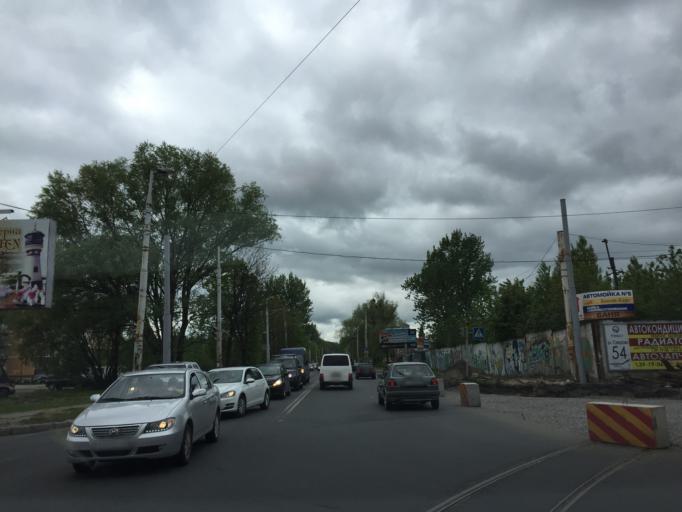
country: RU
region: Kaliningrad
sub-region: Gorod Kaliningrad
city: Kaliningrad
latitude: 54.6906
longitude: 20.4668
